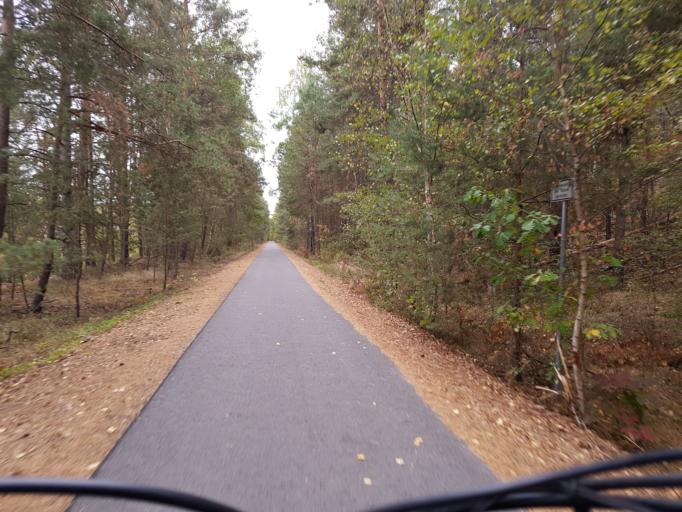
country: DE
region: Brandenburg
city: Trobitz
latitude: 51.5782
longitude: 13.4405
